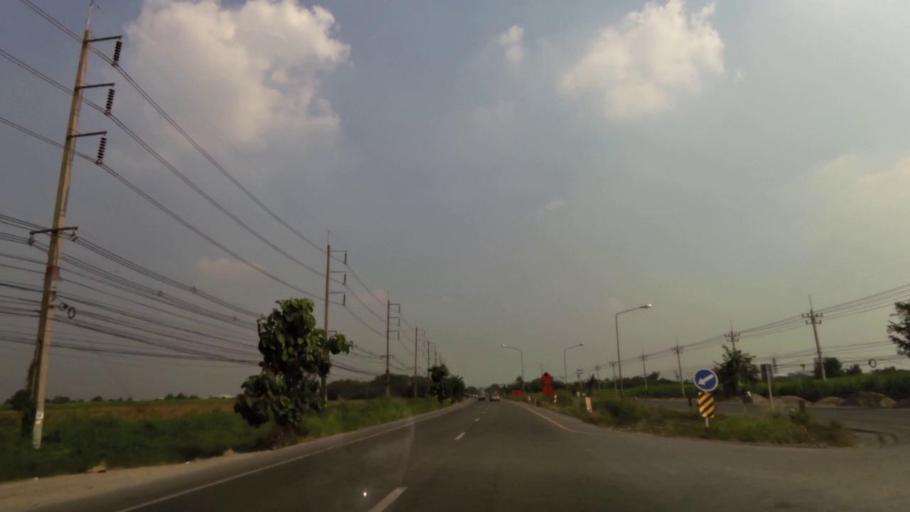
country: TH
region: Chon Buri
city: Ban Bueng
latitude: 13.3002
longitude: 101.1491
